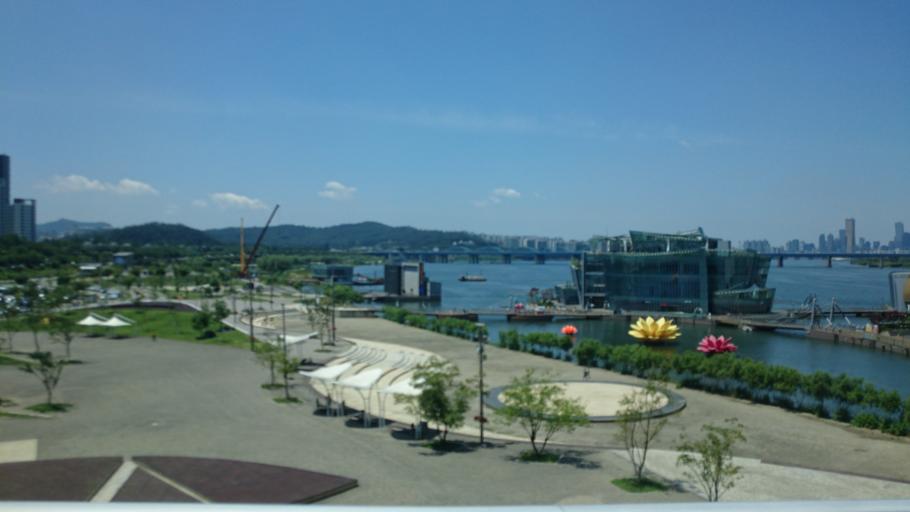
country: KR
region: Seoul
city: Seoul
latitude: 37.5130
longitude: 126.9972
